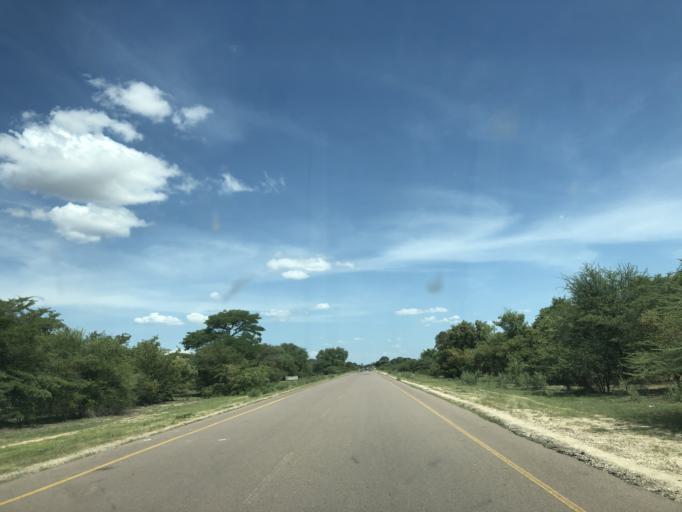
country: AO
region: Cunene
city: Ondjiva
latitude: -16.8718
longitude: 15.4813
